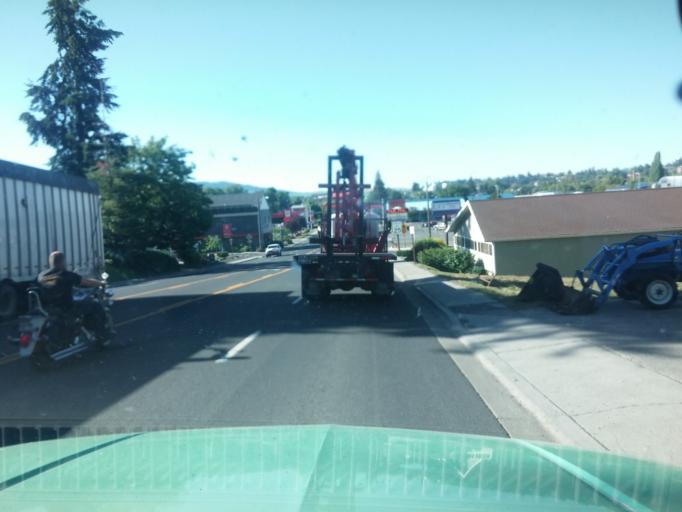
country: US
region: Idaho
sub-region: Latah County
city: Moscow
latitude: 46.7394
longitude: -117.0016
